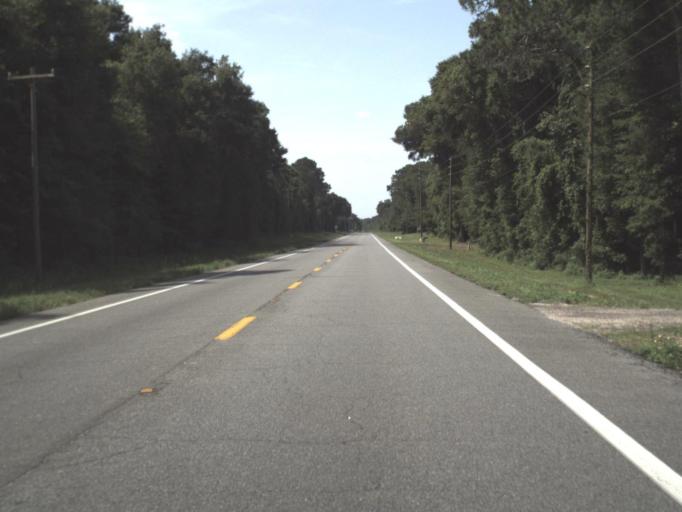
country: US
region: Florida
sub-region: Lafayette County
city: Mayo
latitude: 30.0706
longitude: -83.1743
